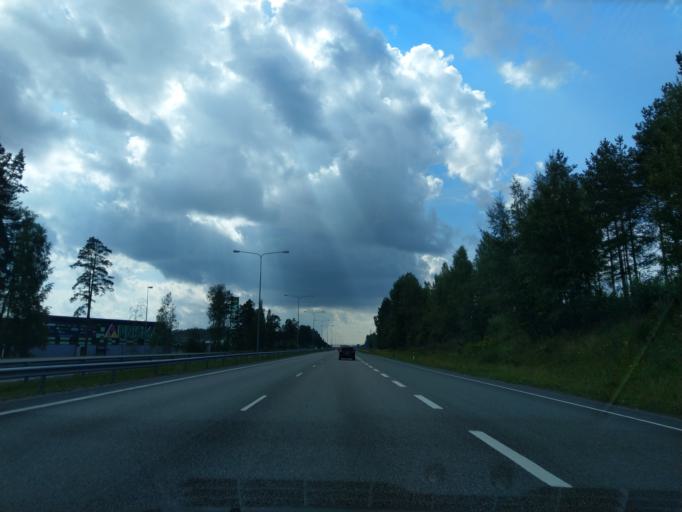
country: FI
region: South Karelia
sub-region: Imatra
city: Imatra
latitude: 61.1913
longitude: 28.7673
